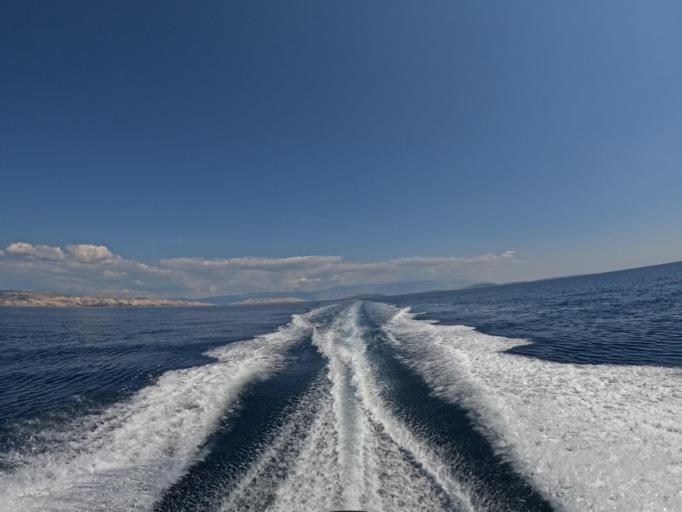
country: HR
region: Primorsko-Goranska
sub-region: Grad Krk
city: Krk
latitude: 44.9208
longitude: 14.5625
